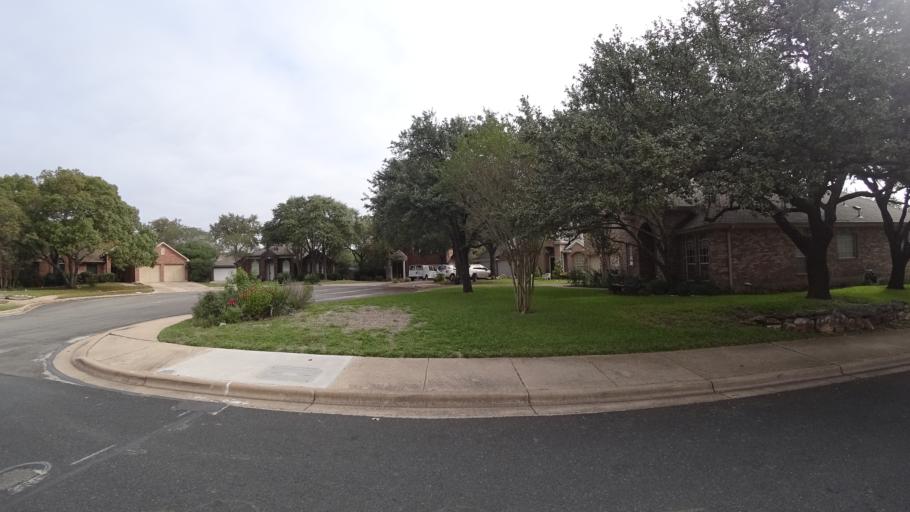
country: US
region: Texas
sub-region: Travis County
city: Shady Hollow
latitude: 30.1941
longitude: -97.8861
